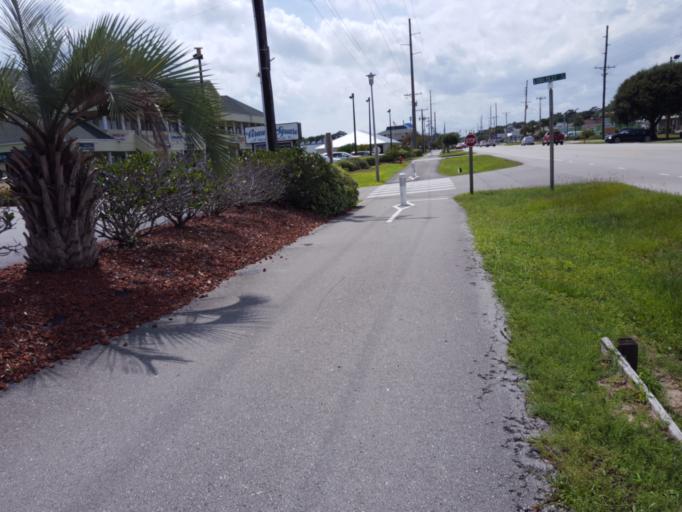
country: US
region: North Carolina
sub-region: Carteret County
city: Cape Carteret
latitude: 34.6654
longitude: -77.0318
